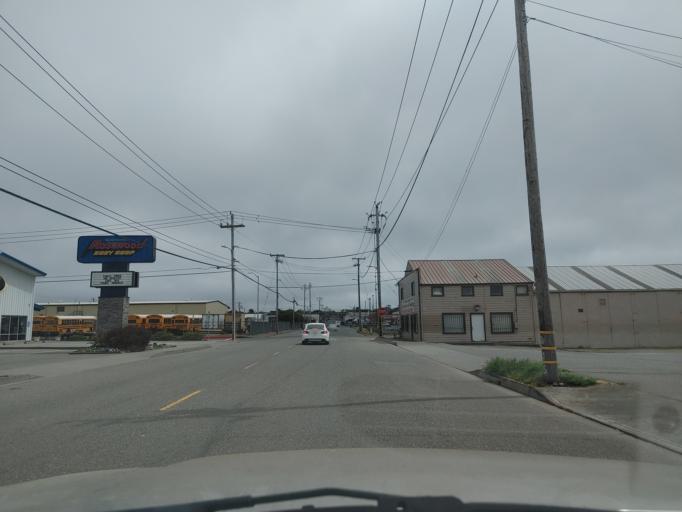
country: US
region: California
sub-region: Humboldt County
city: Eureka
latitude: 40.7941
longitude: -124.1798
